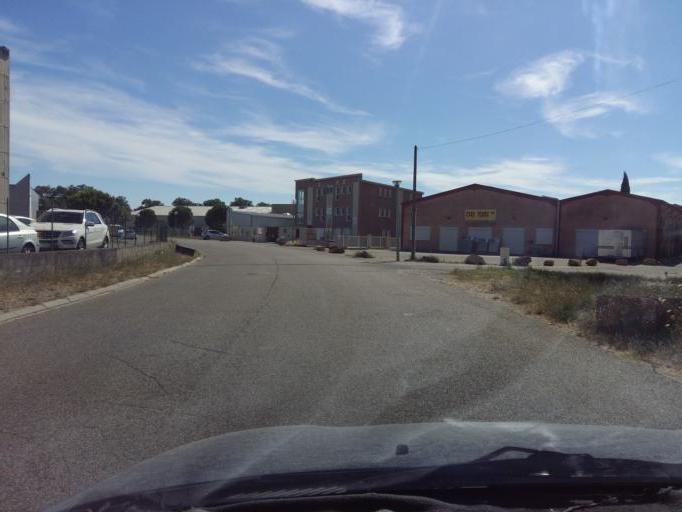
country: FR
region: Provence-Alpes-Cote d'Azur
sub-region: Departement du Vaucluse
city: Piolenc
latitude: 44.1660
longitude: 4.7759
